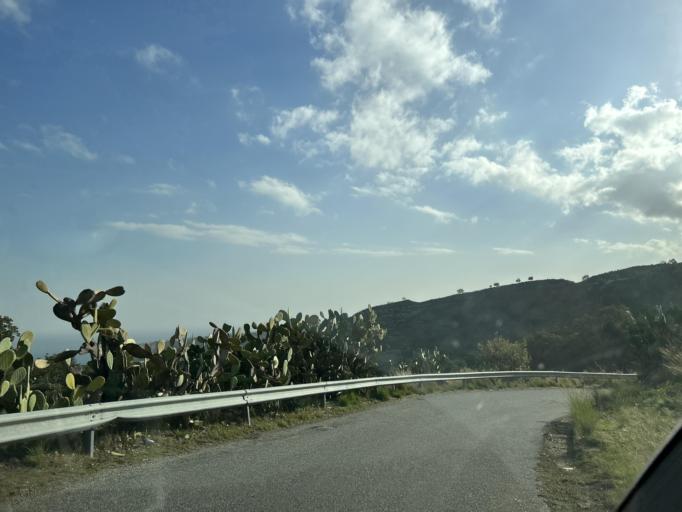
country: IT
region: Calabria
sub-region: Provincia di Catanzaro
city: Montepaone
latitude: 38.7182
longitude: 16.5107
